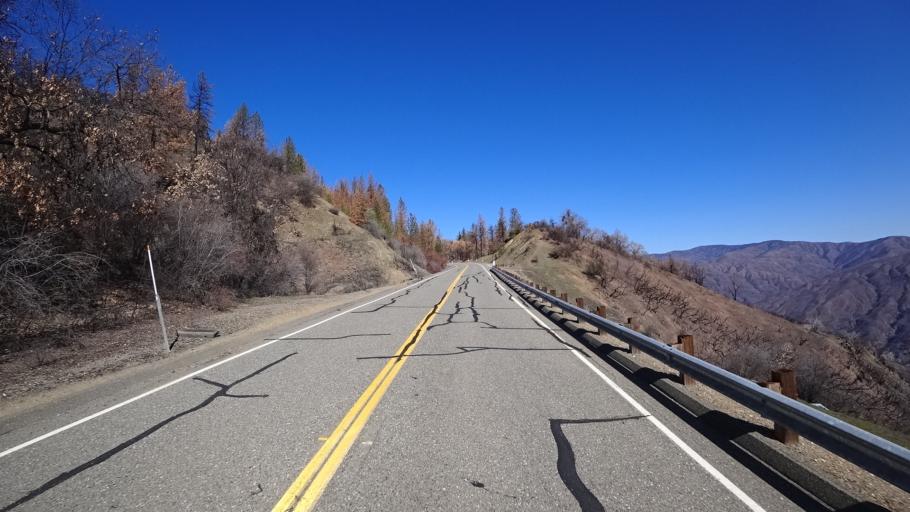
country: US
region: California
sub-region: Tehama County
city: Rancho Tehama Reserve
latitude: 39.6712
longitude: -122.6924
